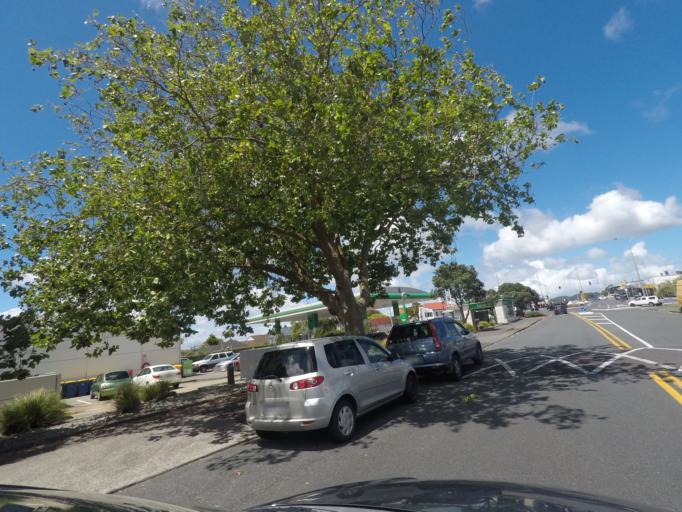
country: NZ
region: Auckland
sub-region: Auckland
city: Rosebank
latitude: -36.8852
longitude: 174.6442
